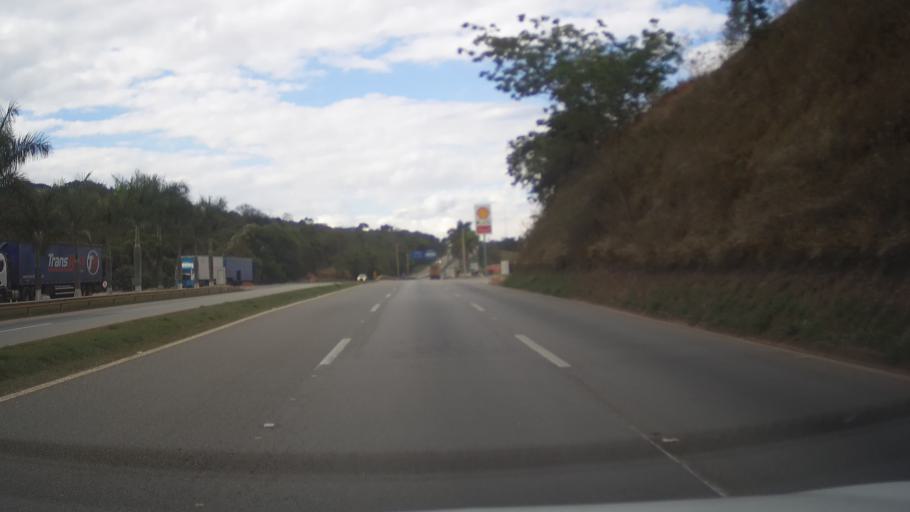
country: BR
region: Minas Gerais
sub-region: Igarape
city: Igarape
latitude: -20.2789
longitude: -44.4277
